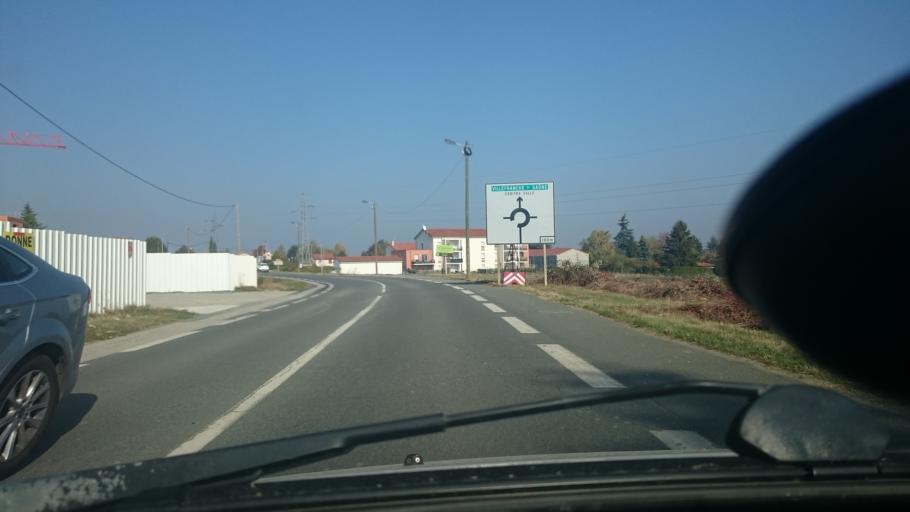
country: FR
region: Rhone-Alpes
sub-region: Departement du Rhone
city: Anse
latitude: 45.9267
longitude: 4.7087
